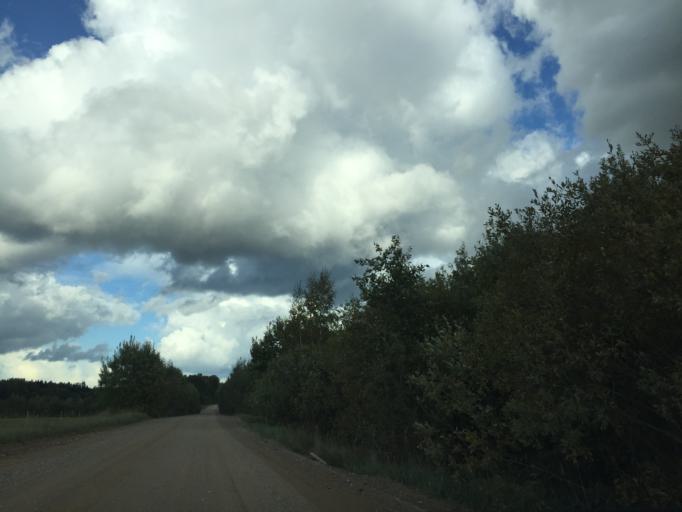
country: LV
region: Malpils
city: Malpils
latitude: 57.0492
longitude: 25.1175
